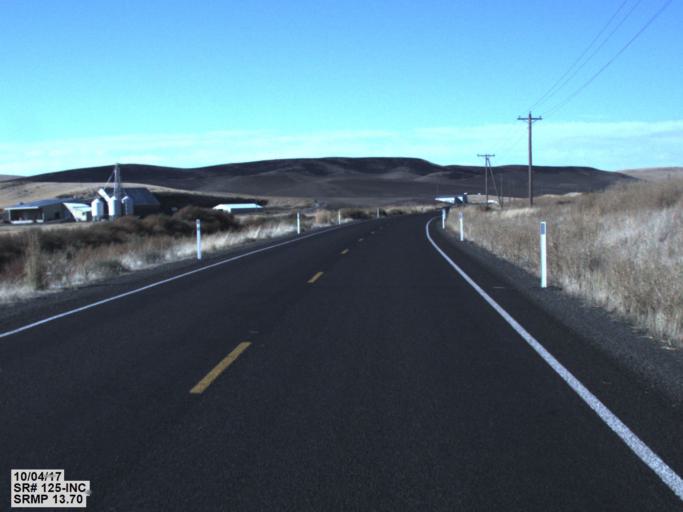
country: US
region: Washington
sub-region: Walla Walla County
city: Walla Walla
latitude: 46.1674
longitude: -118.3820
